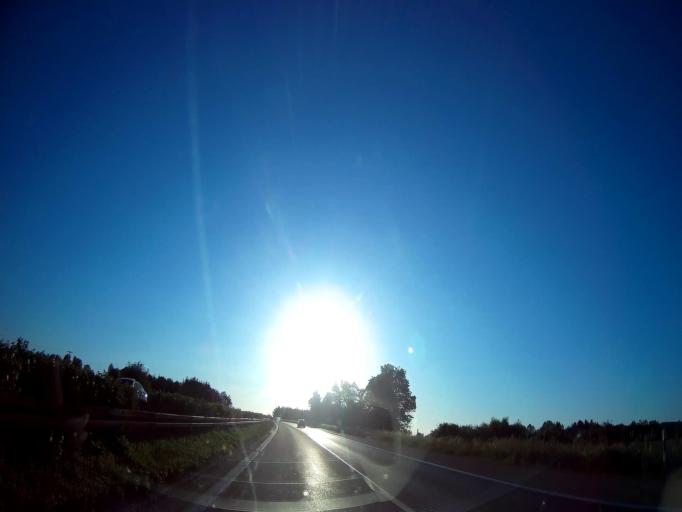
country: DE
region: Bavaria
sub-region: Regierungsbezirk Mittelfranken
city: Altdorf
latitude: 49.3754
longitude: 11.3762
